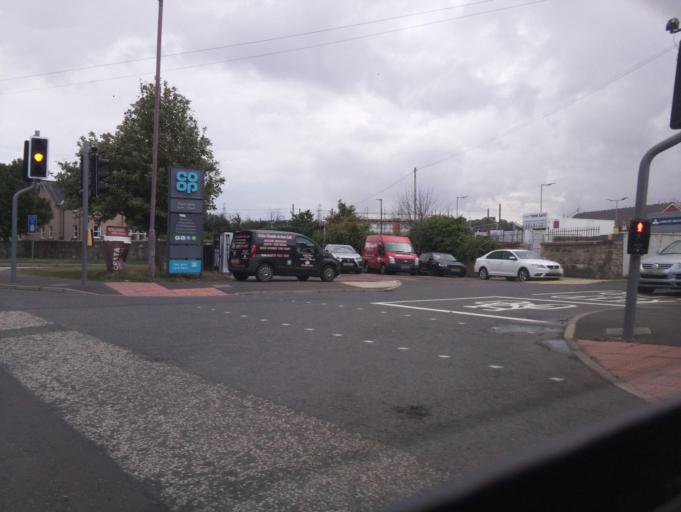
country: GB
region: Scotland
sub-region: East Lothian
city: Prestonpans
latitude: 55.9539
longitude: -2.9762
